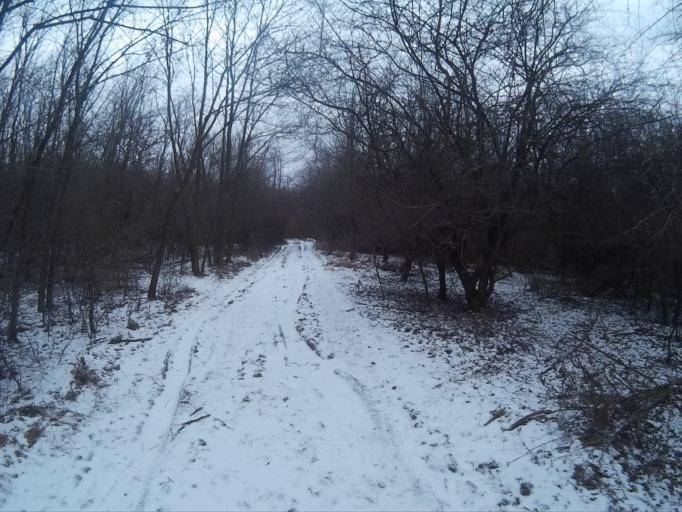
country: HU
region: Borsod-Abauj-Zemplen
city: Halmaj
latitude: 48.3721
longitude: 20.9982
